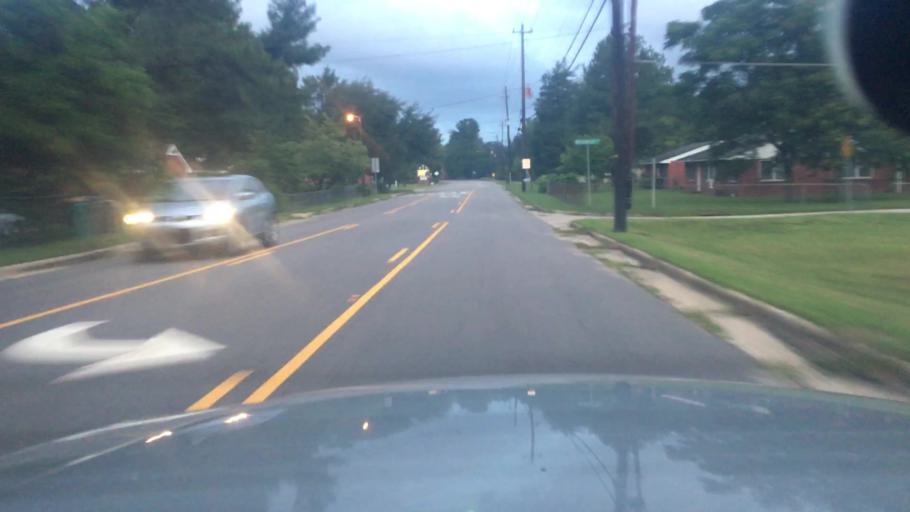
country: US
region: North Carolina
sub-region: Cumberland County
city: Hope Mills
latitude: 34.9660
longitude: -78.9373
